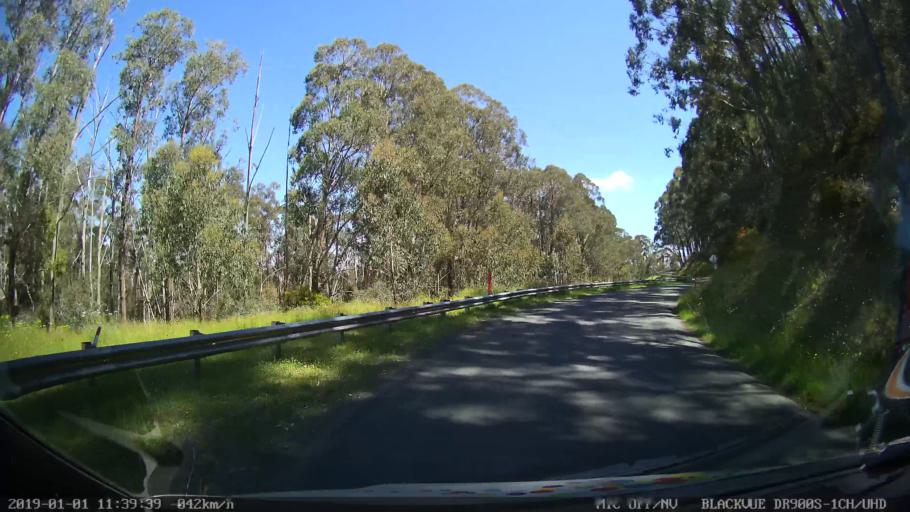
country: AU
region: New South Wales
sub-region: Snowy River
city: Jindabyne
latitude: -35.9252
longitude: 148.3861
